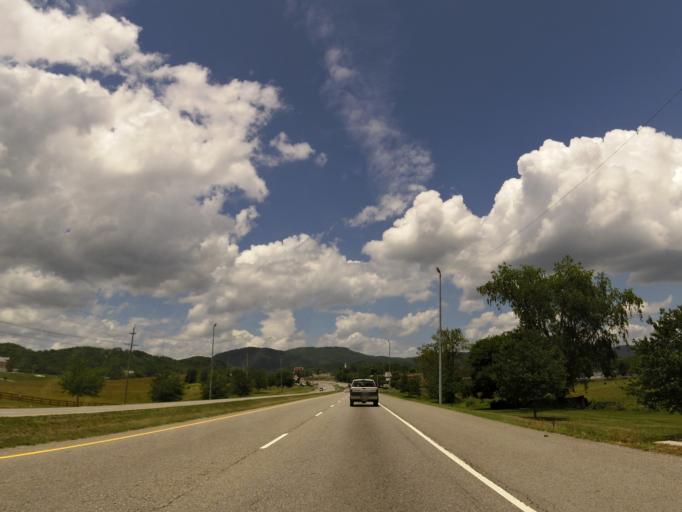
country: US
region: Tennessee
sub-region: Claiborne County
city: Harrogate
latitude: 36.5699
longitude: -83.6534
